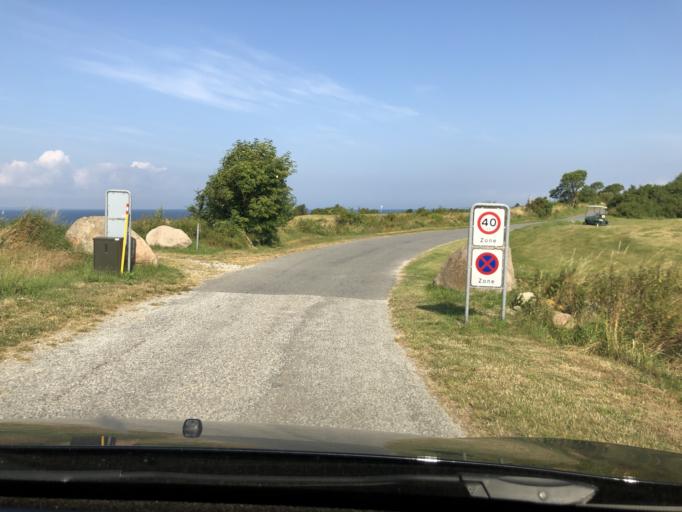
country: DK
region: South Denmark
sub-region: Faaborg-Midtfyn Kommune
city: Faaborg
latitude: 54.9625
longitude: 10.2128
